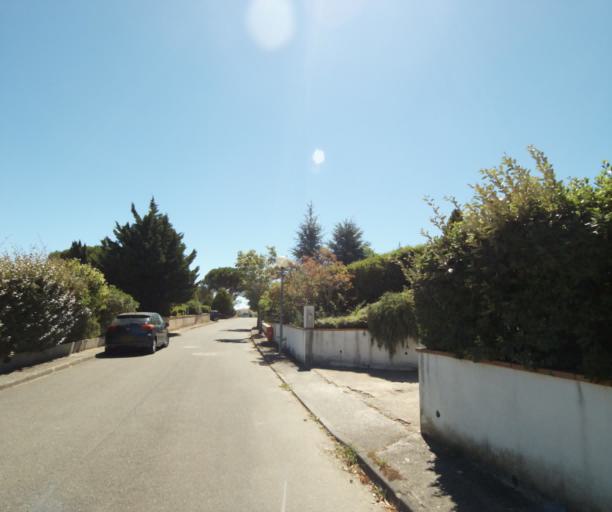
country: FR
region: Midi-Pyrenees
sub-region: Departement de la Haute-Garonne
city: Castanet-Tolosan
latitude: 43.5108
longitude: 1.4985
